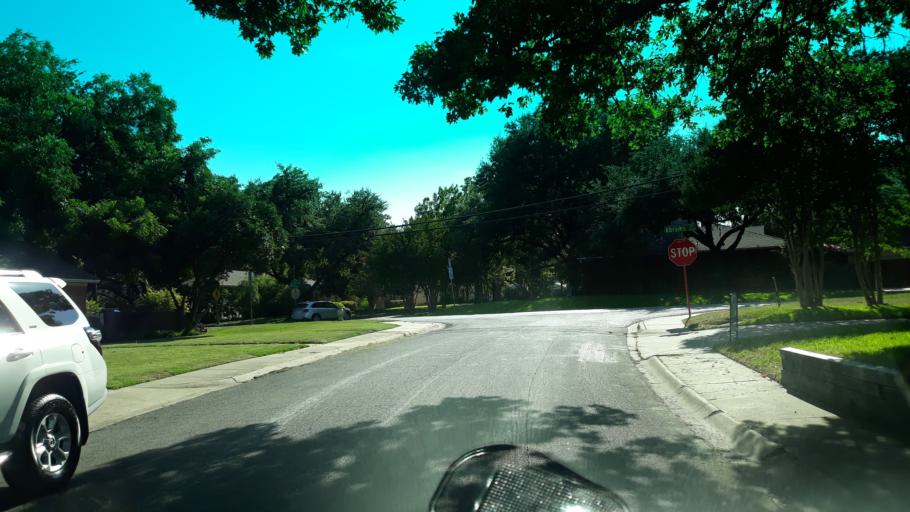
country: US
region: Texas
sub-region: Dallas County
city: Highland Park
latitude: 32.8259
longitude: -96.7525
